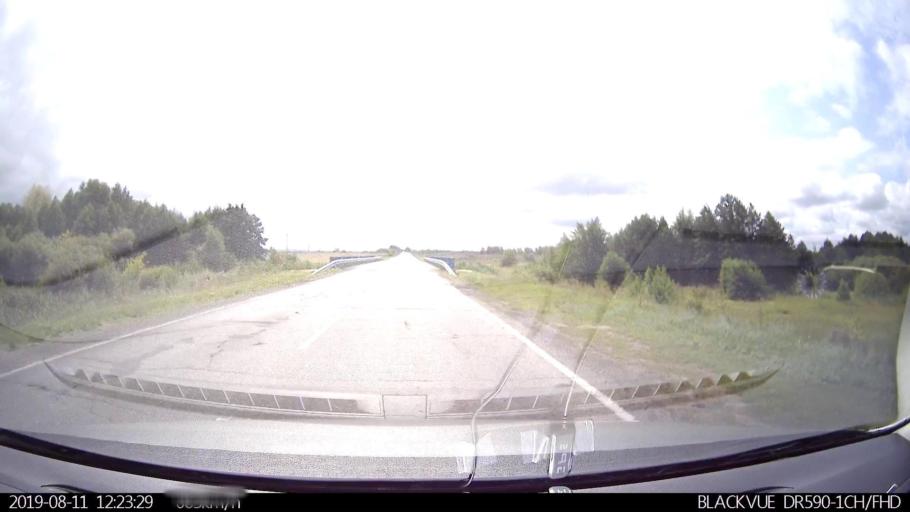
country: RU
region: Ulyanovsk
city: Ignatovka
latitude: 53.8946
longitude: 47.9504
